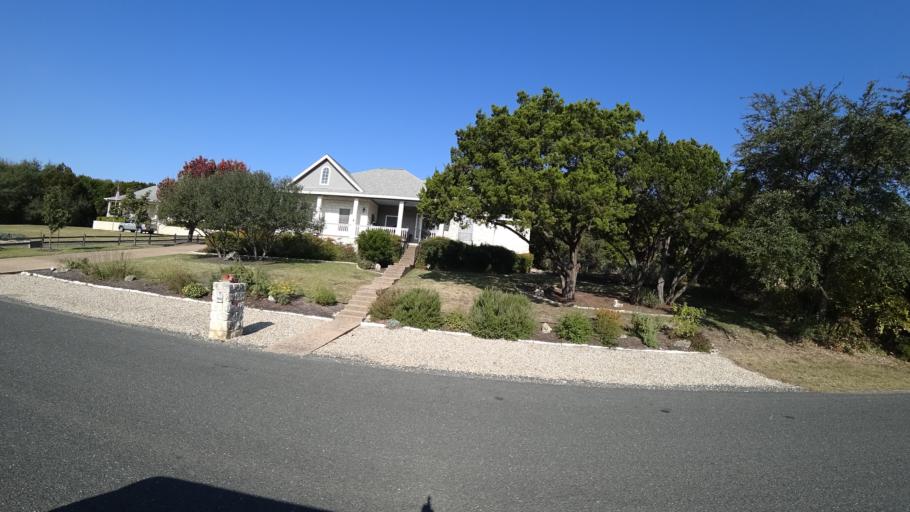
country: US
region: Texas
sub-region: Travis County
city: West Lake Hills
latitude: 30.3704
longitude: -97.8224
